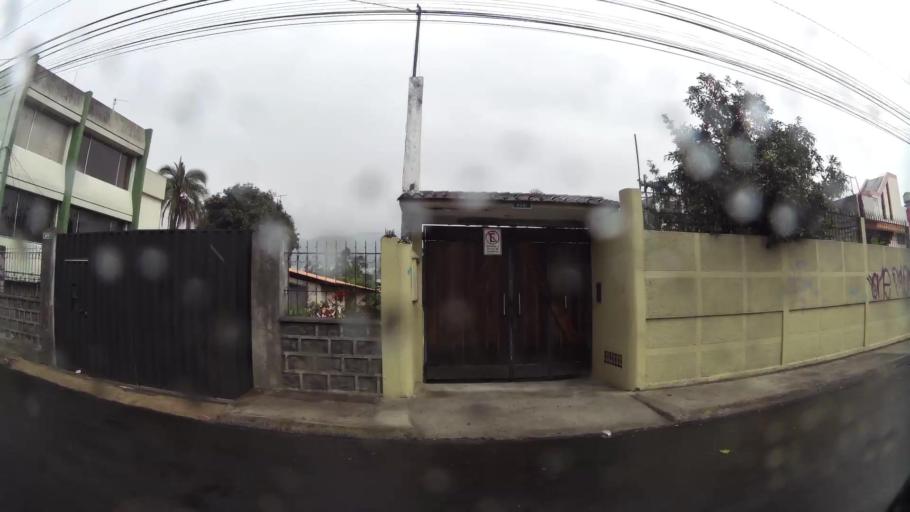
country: EC
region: Pichincha
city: Sangolqui
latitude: -0.2910
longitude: -78.4770
